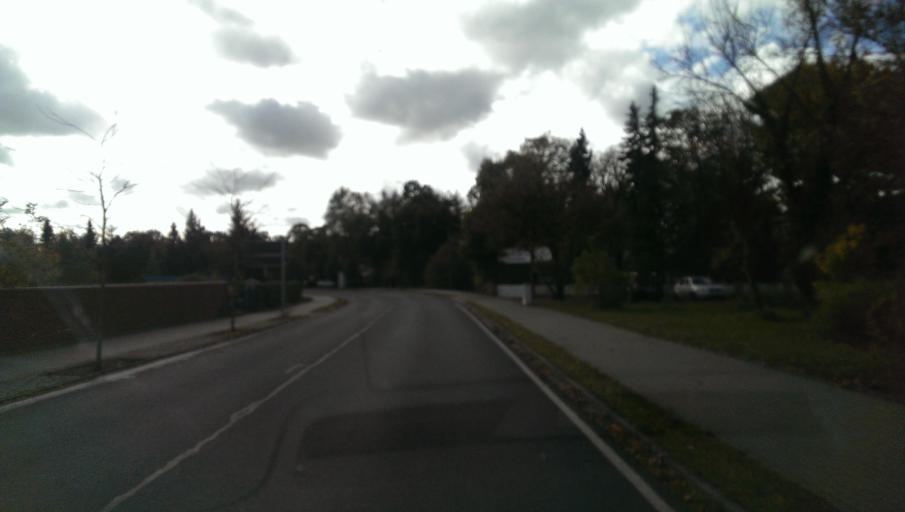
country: DE
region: Brandenburg
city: Luckenwalde
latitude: 52.0785
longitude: 13.1588
